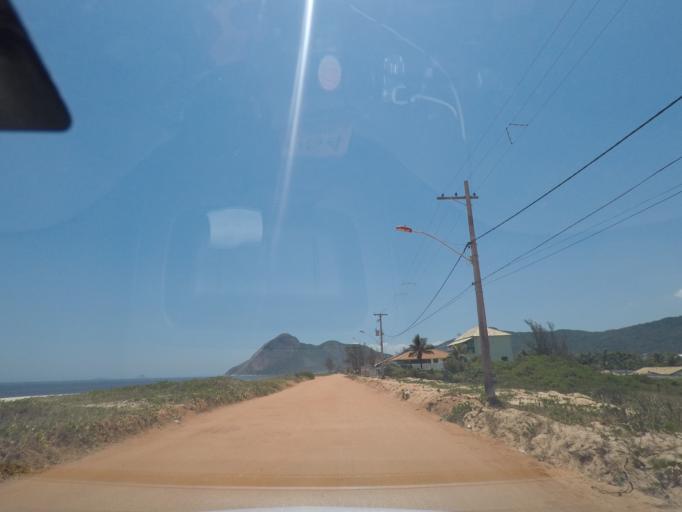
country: BR
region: Rio de Janeiro
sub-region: Niteroi
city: Niteroi
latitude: -22.9690
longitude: -42.9836
